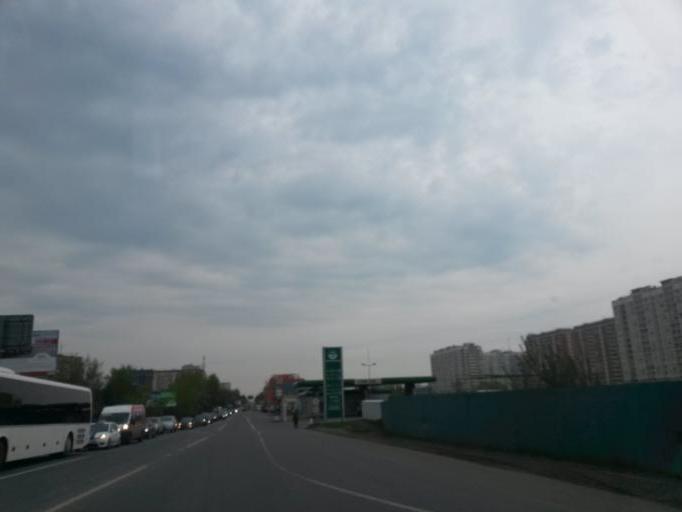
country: RU
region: Moskovskaya
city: Shcherbinka
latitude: 55.5002
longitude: 37.5713
